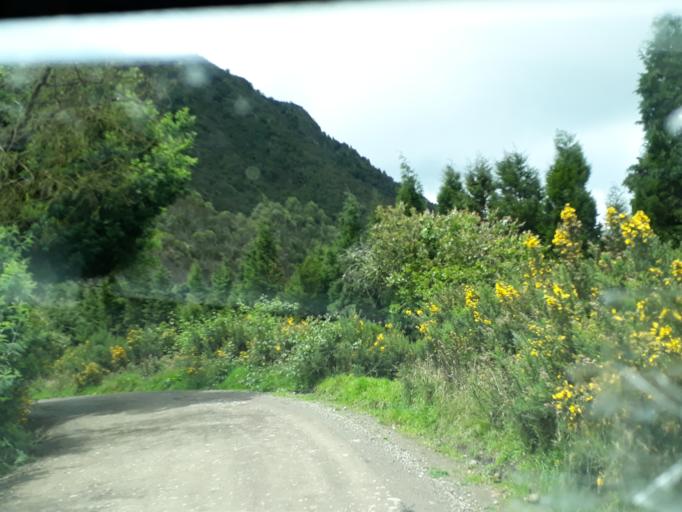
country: CO
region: Cundinamarca
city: Cogua
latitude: 5.1648
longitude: -73.9978
